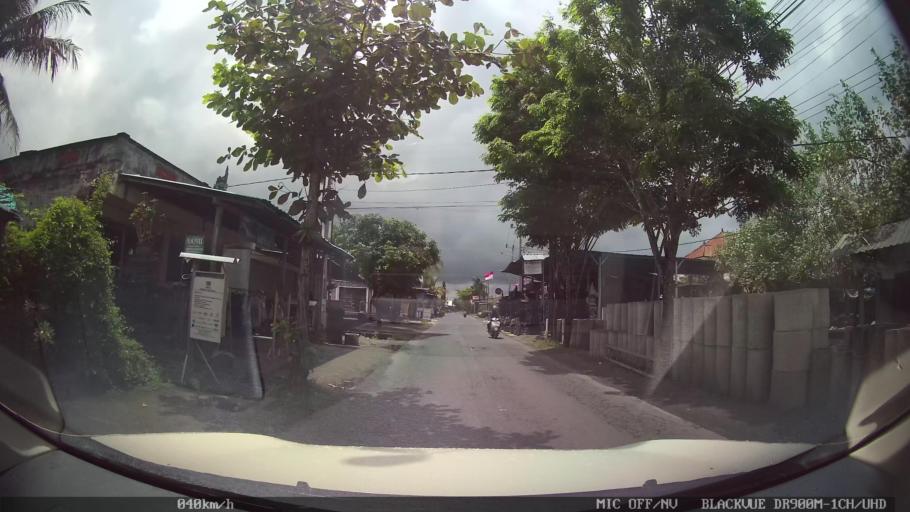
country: ID
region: Bali
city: Banjar Pekenjelodan
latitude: -8.5643
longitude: 115.1856
